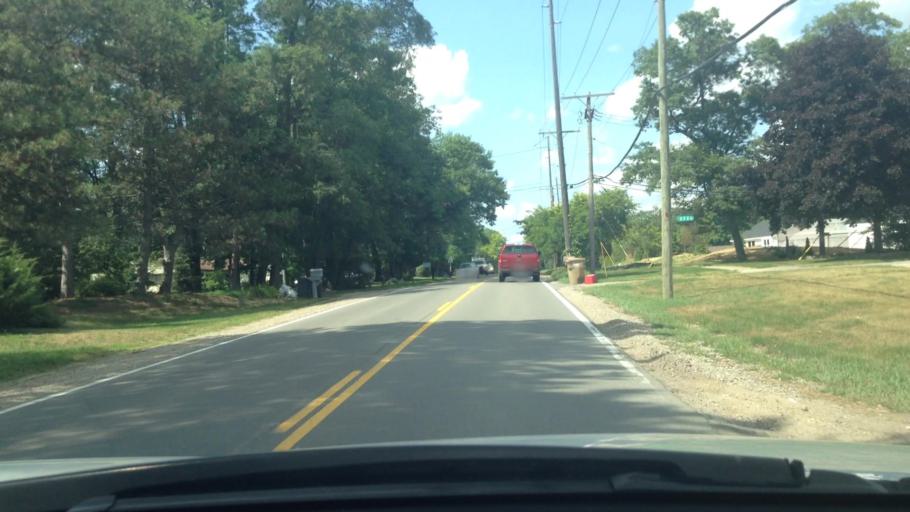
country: US
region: Michigan
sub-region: Oakland County
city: Waterford
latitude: 42.6936
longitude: -83.3483
